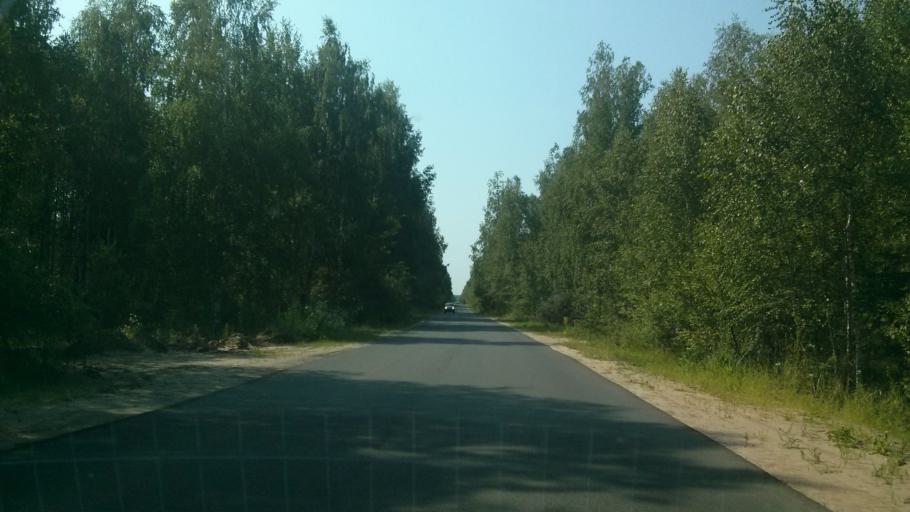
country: RU
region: Vladimir
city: Murom
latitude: 55.5195
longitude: 42.0203
